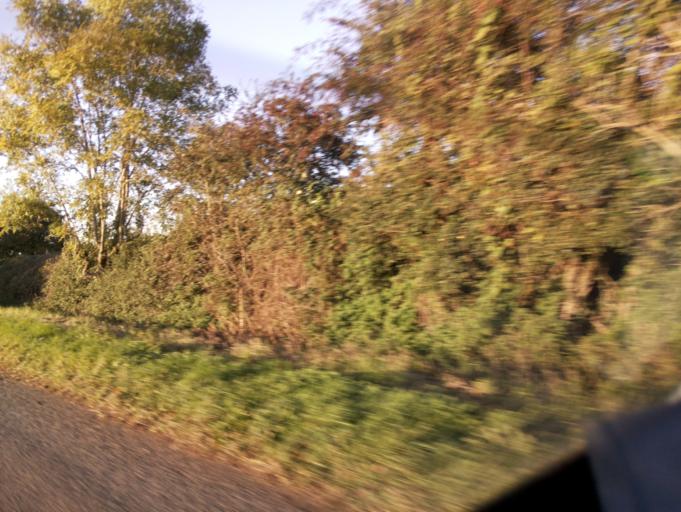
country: GB
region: England
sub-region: Worcestershire
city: Upton upon Severn
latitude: 52.0014
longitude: -2.2352
